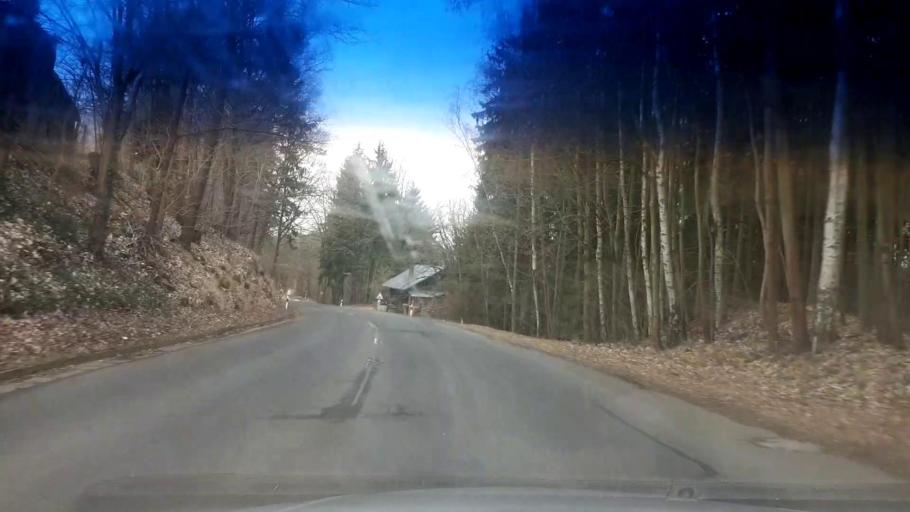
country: DE
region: Bavaria
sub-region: Upper Franconia
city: Schirnding
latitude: 50.0833
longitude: 12.2361
